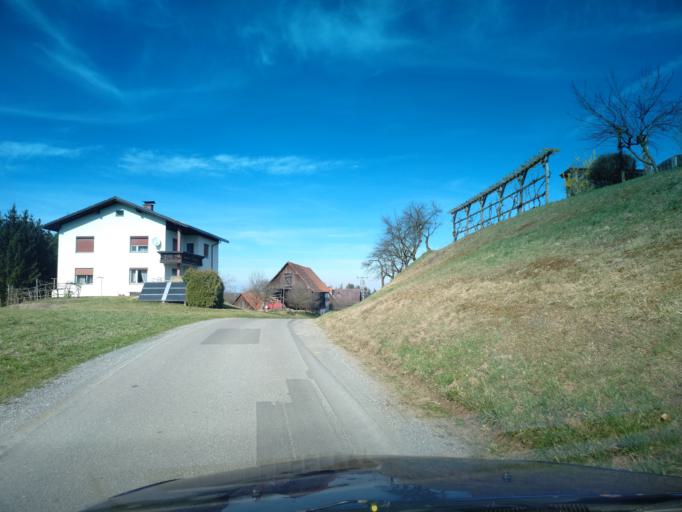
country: AT
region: Styria
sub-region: Politischer Bezirk Deutschlandsberg
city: Unterbergla
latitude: 46.7917
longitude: 15.3022
